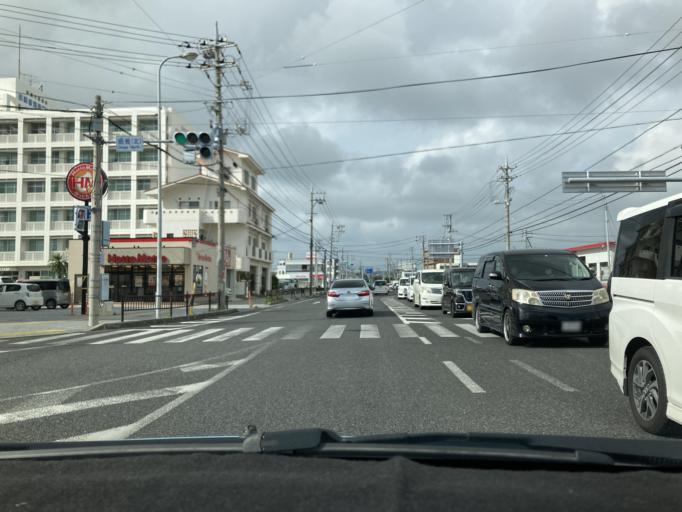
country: JP
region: Okinawa
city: Tomigusuku
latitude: 26.1622
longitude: 127.6692
